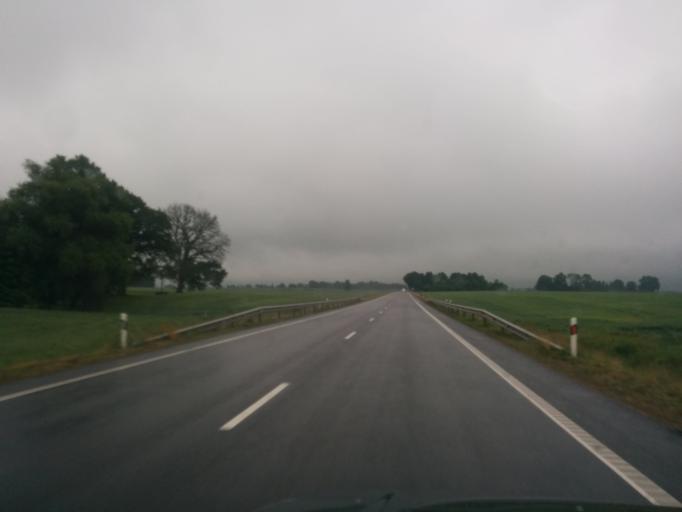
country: LT
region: Panevezys
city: Pasvalys
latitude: 56.2005
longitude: 24.4289
